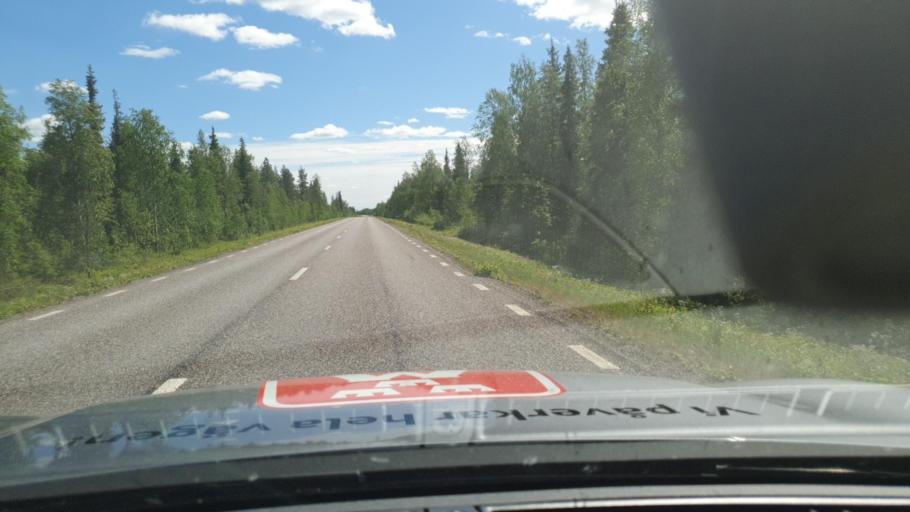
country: SE
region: Norrbotten
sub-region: Pajala Kommun
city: Pajala
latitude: 67.1367
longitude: 23.5800
